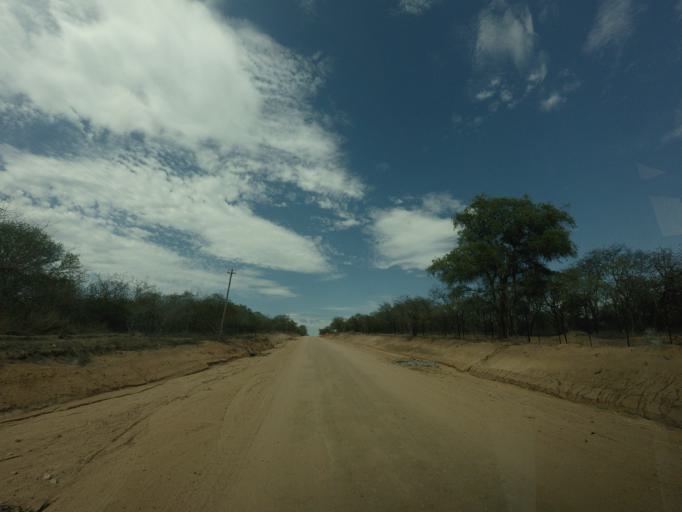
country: ZA
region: Limpopo
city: Thulamahashi
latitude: -24.5416
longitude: 31.0871
